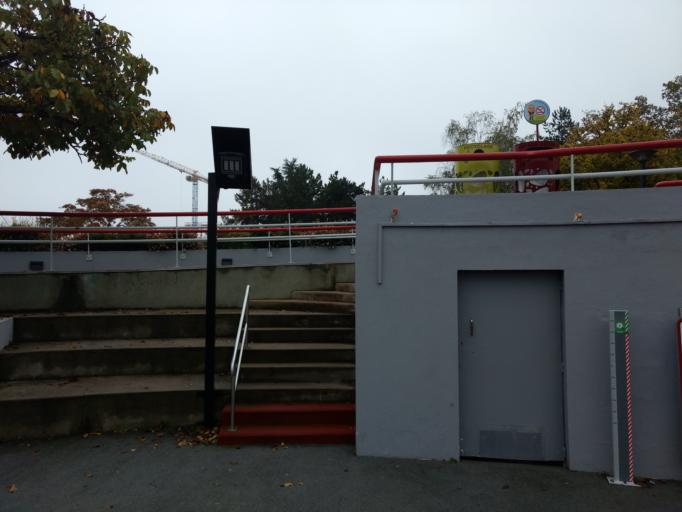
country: FR
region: Poitou-Charentes
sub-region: Departement de la Vienne
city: Jaunay-Clan
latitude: 46.6680
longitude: 0.3680
